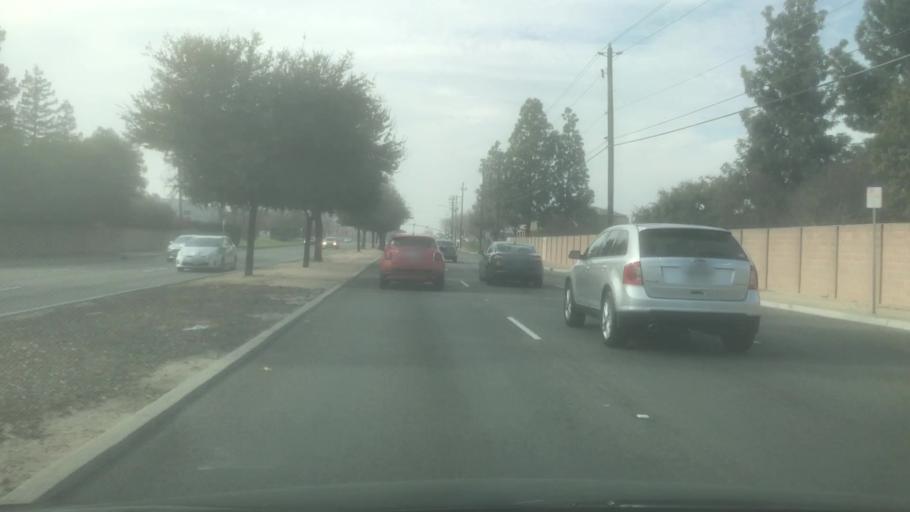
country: US
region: California
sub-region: Fresno County
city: Fresno
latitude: 36.8373
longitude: -119.8229
